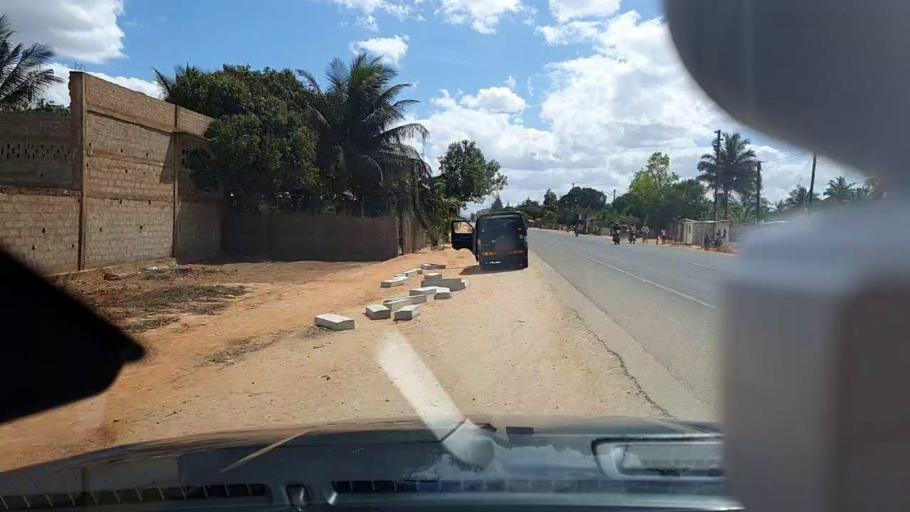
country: MZ
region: Nampula
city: Nampula
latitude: -15.1484
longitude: 39.2994
